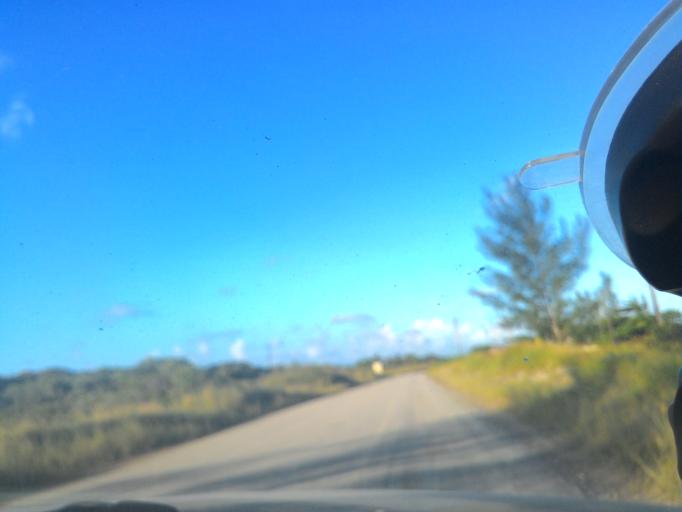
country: BR
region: Sao Paulo
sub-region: Pariquera-Acu
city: Pariquera Acu
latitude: -24.8661
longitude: -47.7172
